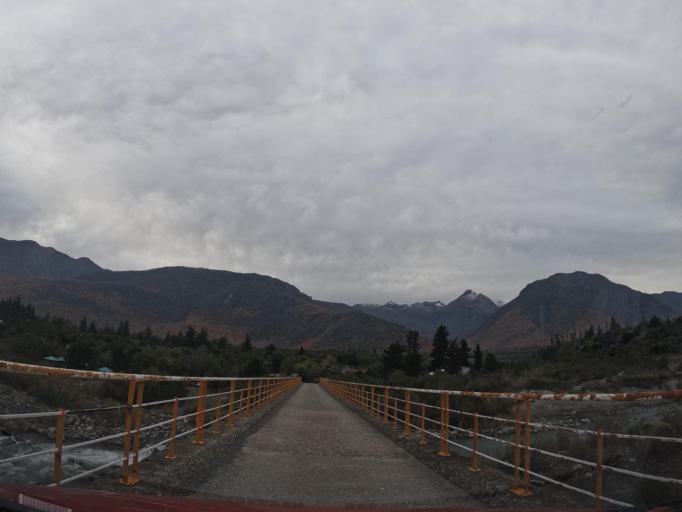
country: CL
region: Maule
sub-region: Provincia de Linares
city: Colbun
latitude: -35.7053
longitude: -71.0778
